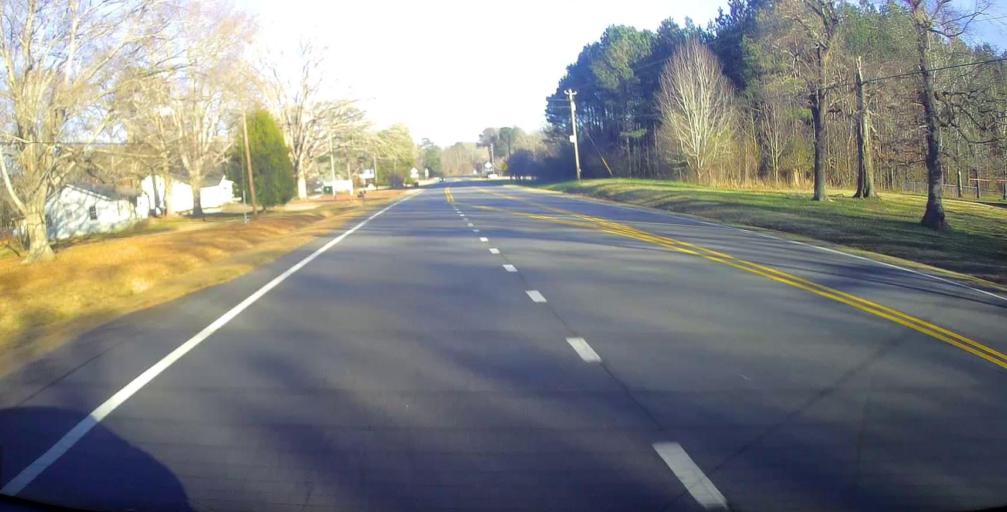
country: US
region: Georgia
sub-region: Meriwether County
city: Manchester
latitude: 32.8770
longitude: -84.6433
